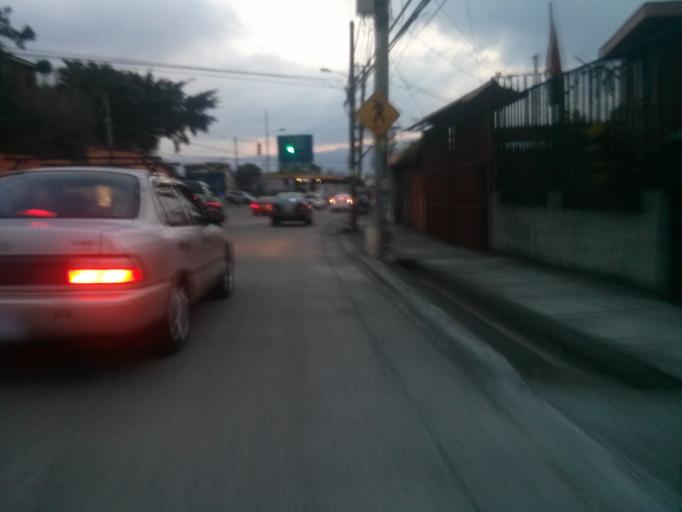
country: CR
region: San Jose
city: San Pedro
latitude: 9.9163
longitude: -84.0550
